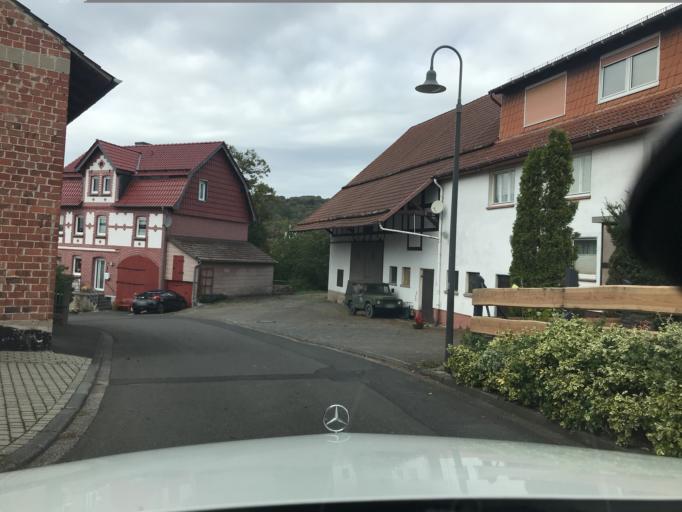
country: DE
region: Hesse
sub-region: Regierungsbezirk Kassel
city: Grossalmerode
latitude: 51.2323
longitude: 9.8156
